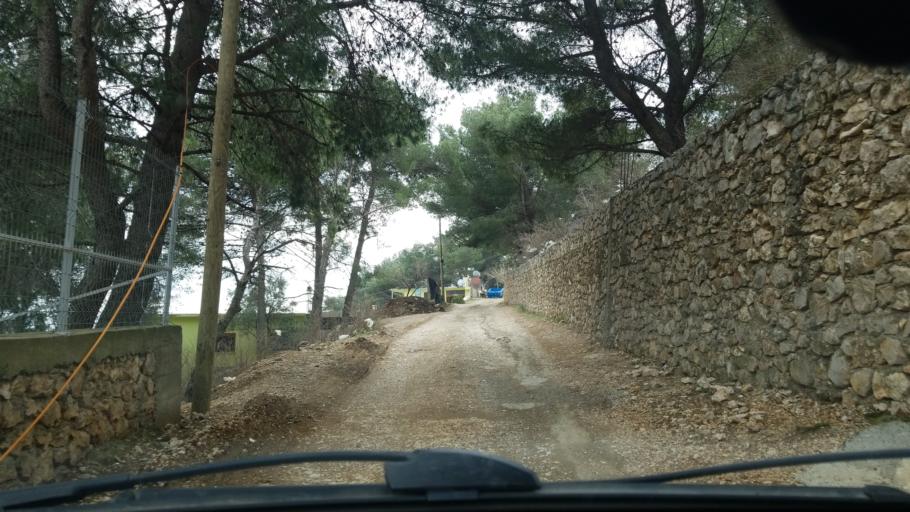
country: AL
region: Lezhe
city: Shengjin
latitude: 41.8158
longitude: 19.5838
